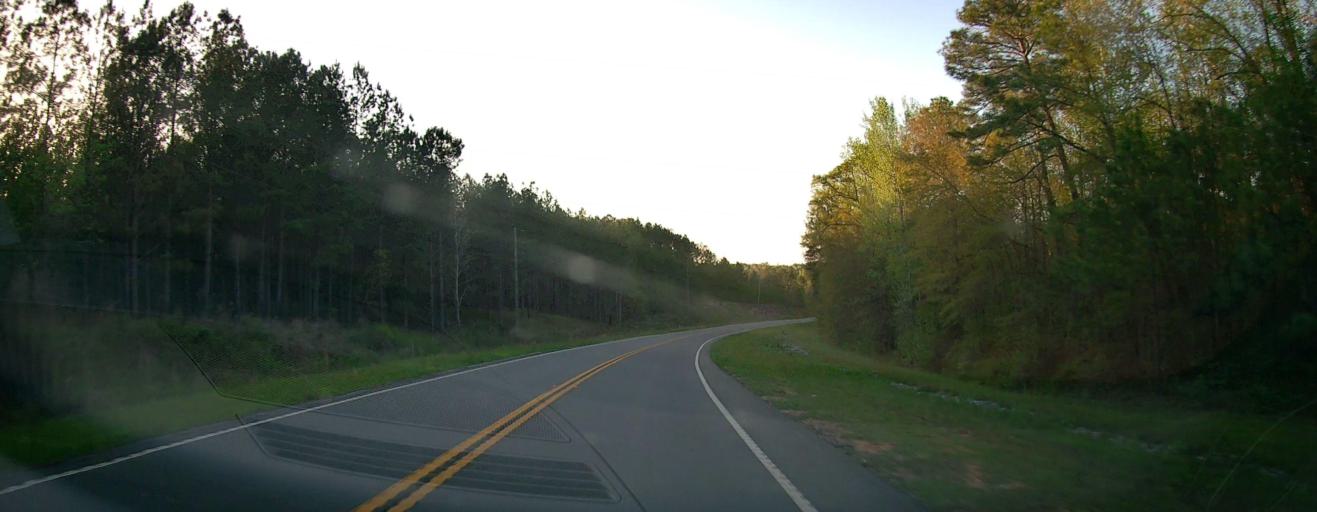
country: US
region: Georgia
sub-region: Talbot County
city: Talbotton
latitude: 32.5459
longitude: -84.5317
